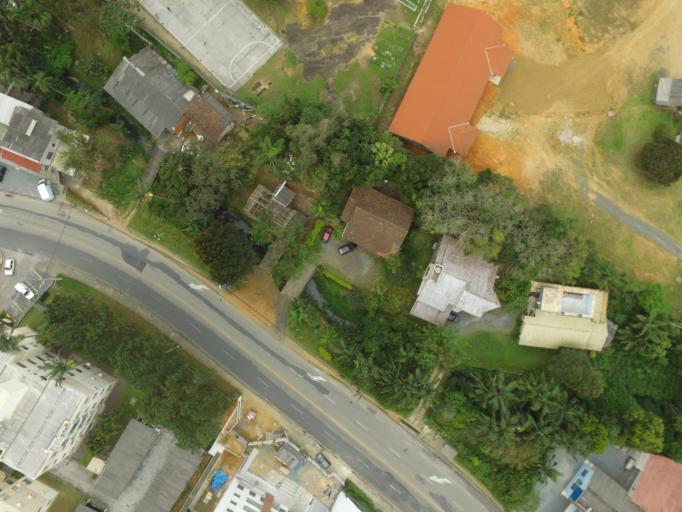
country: BR
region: Santa Catarina
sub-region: Blumenau
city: Blumenau
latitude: -26.8946
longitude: -49.1312
